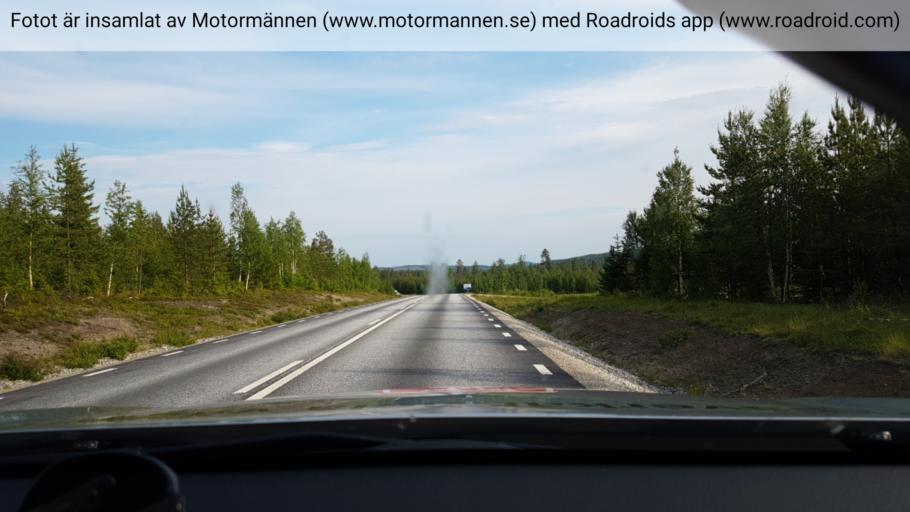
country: SE
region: Vaesterbotten
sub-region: Vindelns Kommun
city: Vindeln
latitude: 64.0647
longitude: 19.6395
